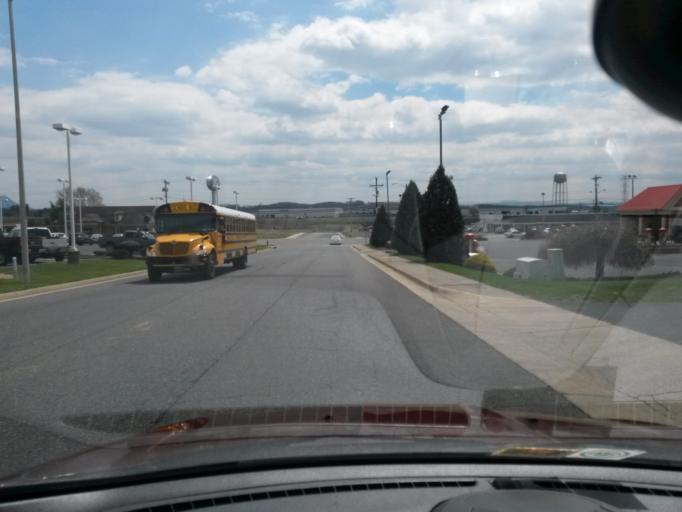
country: US
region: Virginia
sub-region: Rockingham County
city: Dayton
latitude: 38.4102
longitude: -78.9056
